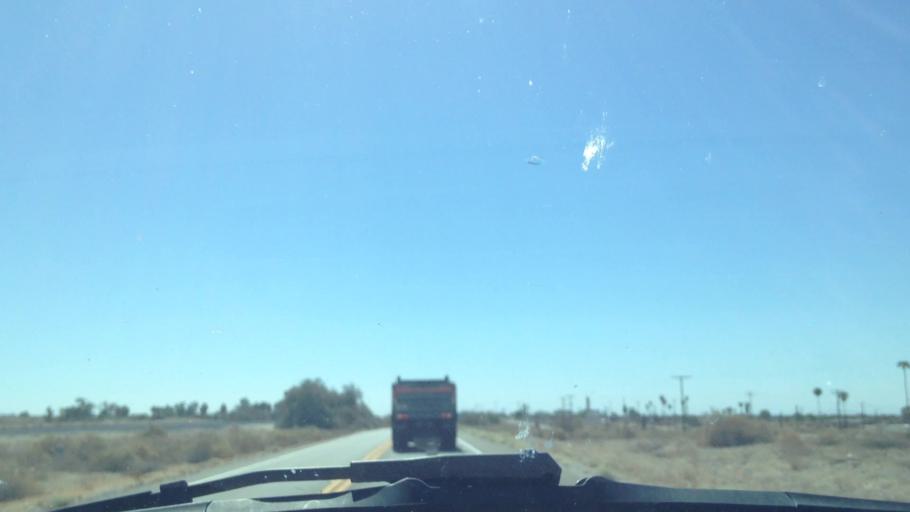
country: US
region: California
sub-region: Riverside County
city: Mecca
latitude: 33.5234
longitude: -115.9376
